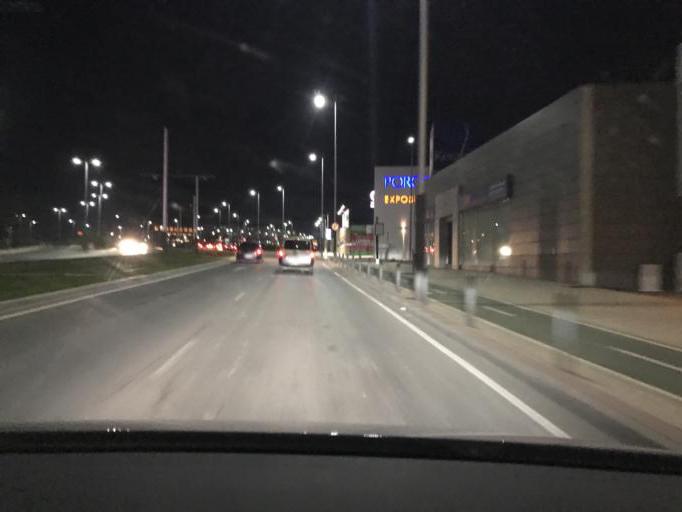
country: ES
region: Andalusia
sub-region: Provincia de Jaen
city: Jaen
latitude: 37.7934
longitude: -3.7805
